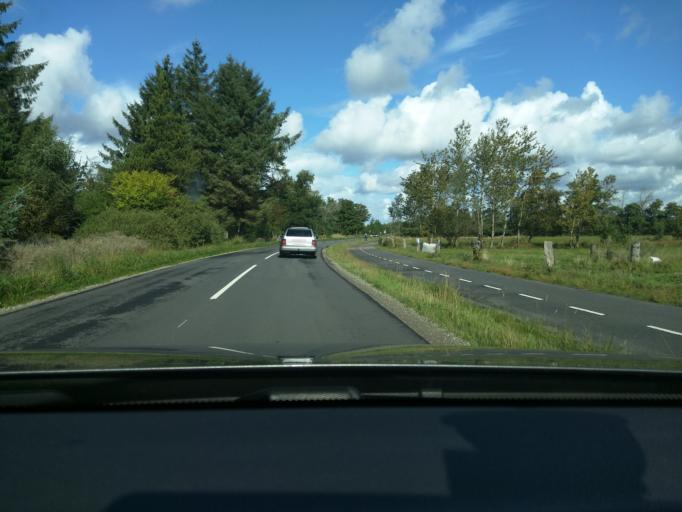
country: DK
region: South Denmark
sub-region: Varde Kommune
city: Oksbol
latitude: 55.5605
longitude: 8.2260
